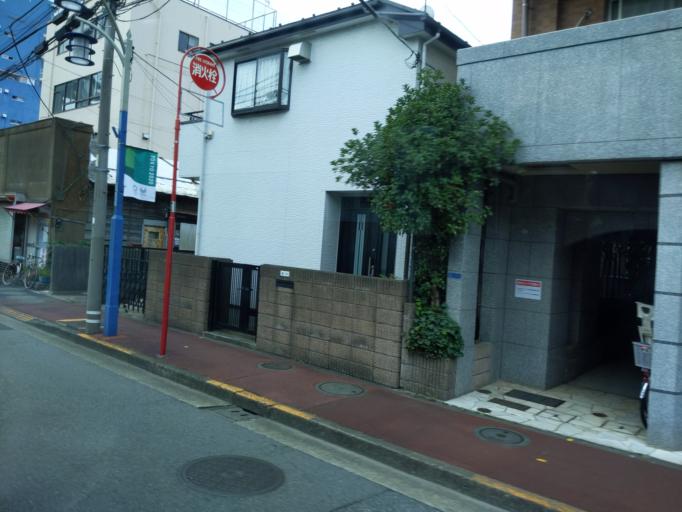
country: JP
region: Kanagawa
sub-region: Kawasaki-shi
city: Kawasaki
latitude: 35.5824
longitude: 139.6969
